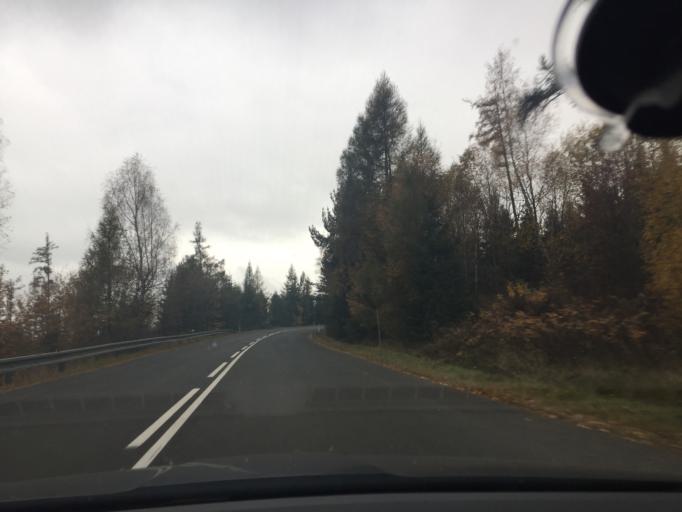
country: SK
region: Presovsky
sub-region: Okres Poprad
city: Svit
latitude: 49.1185
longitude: 20.1673
